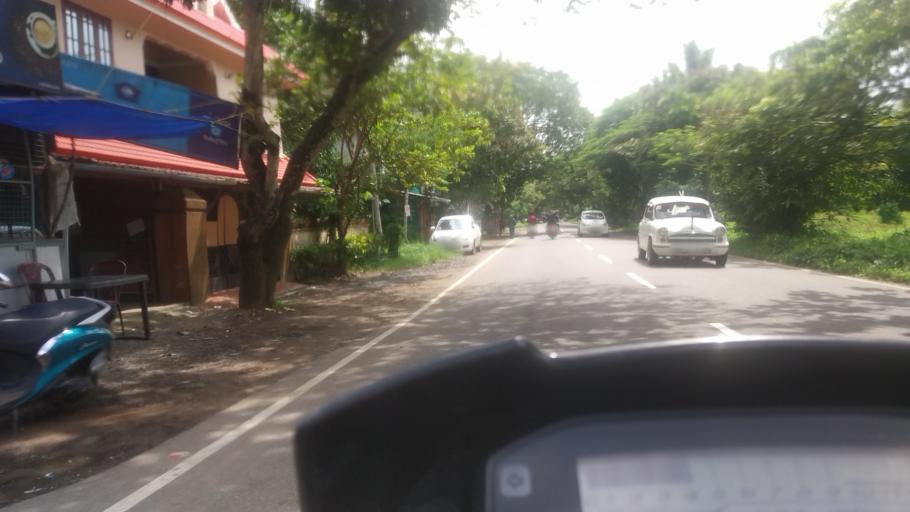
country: IN
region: Kerala
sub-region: Ernakulam
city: Aluva
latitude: 10.1305
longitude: 76.2915
